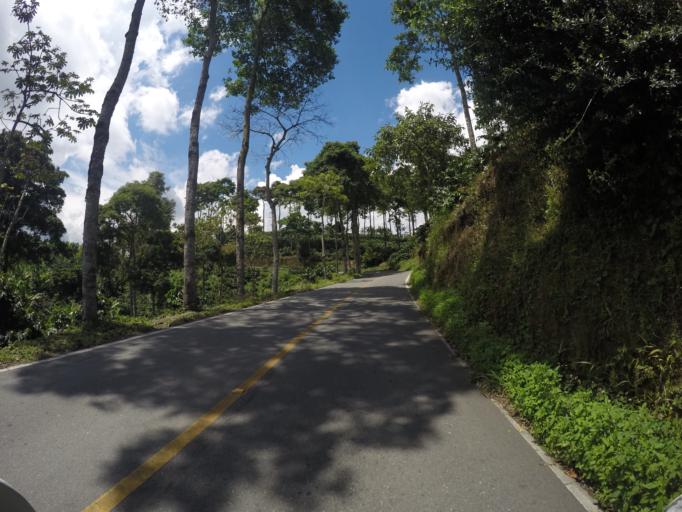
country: CO
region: Quindio
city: Quimbaya
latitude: 4.6303
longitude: -75.7196
